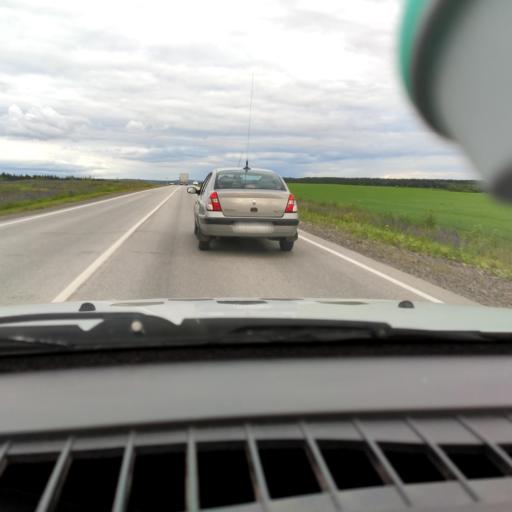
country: RU
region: Perm
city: Lyamino
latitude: 58.3217
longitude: 57.7087
